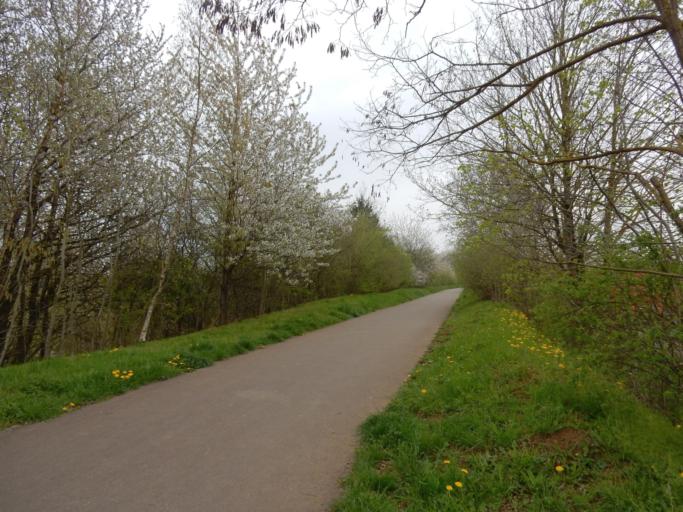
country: LU
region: Luxembourg
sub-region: Canton d'Esch-sur-Alzette
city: Petange
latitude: 49.5613
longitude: 5.8834
